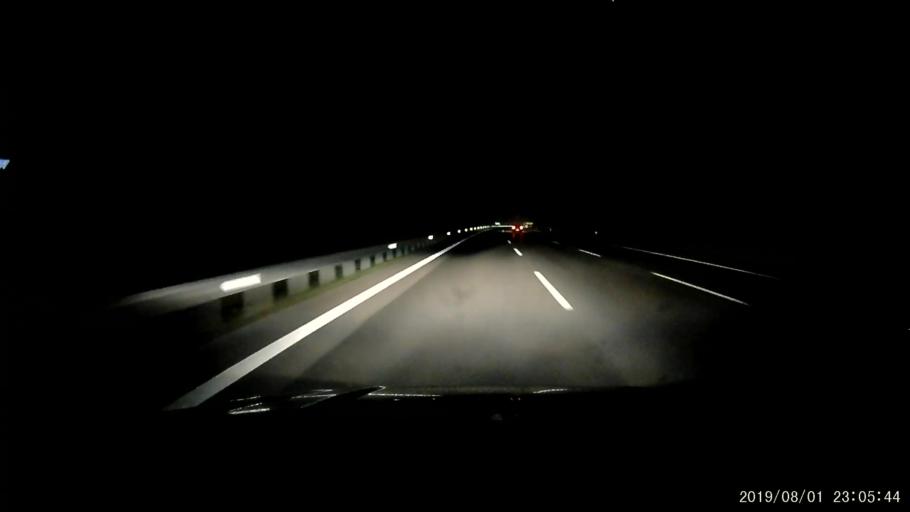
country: TR
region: Tekirdag
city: Beyazkoy
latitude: 41.3564
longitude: 27.6406
